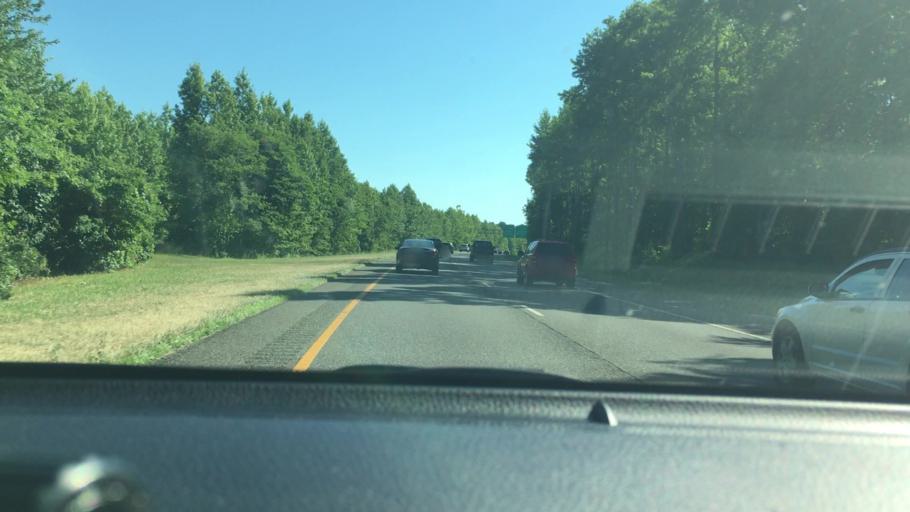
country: US
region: New Jersey
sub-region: Gloucester County
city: Pitman
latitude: 39.7611
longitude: -75.1239
